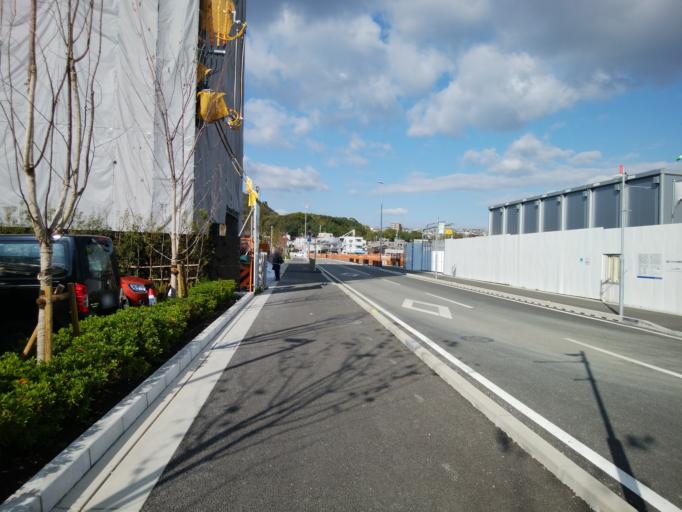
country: JP
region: Osaka
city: Ikeda
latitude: 34.8353
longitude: 135.4188
